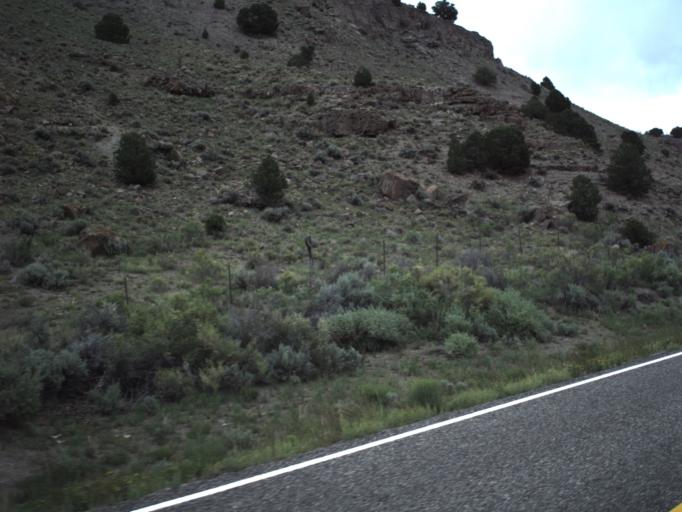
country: US
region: Utah
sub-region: Piute County
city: Junction
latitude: 38.1778
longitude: -112.0721
